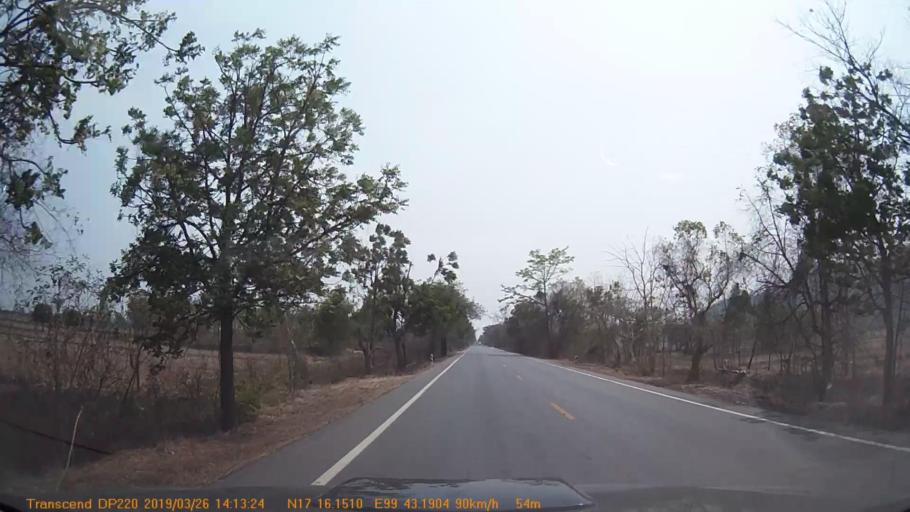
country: TH
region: Sukhothai
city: Sawankhalok
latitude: 17.2688
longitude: 99.7197
